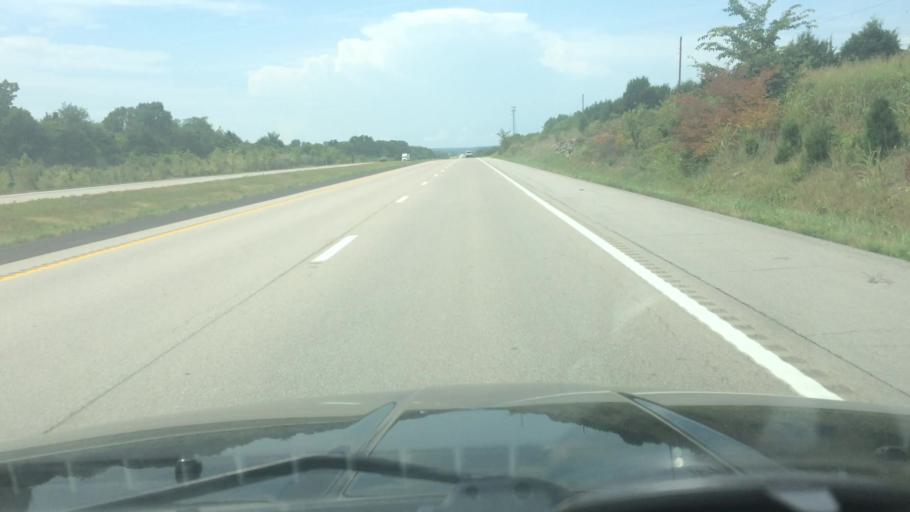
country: US
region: Missouri
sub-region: Polk County
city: Humansville
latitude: 37.7734
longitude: -93.5683
